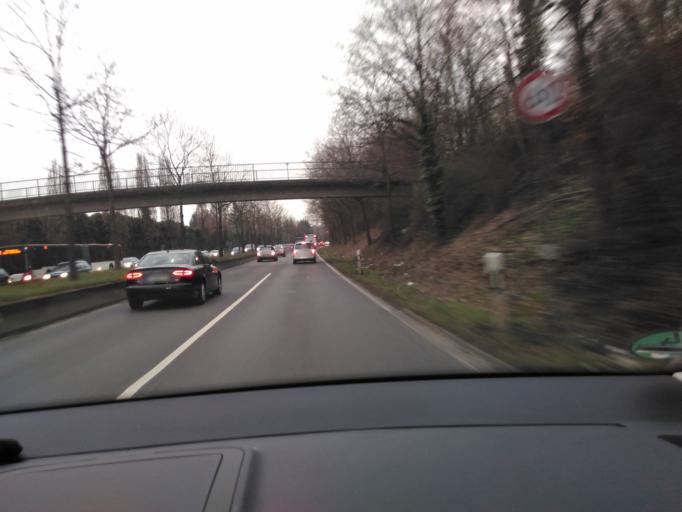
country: DE
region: North Rhine-Westphalia
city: Opladen
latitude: 51.0371
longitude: 7.0478
